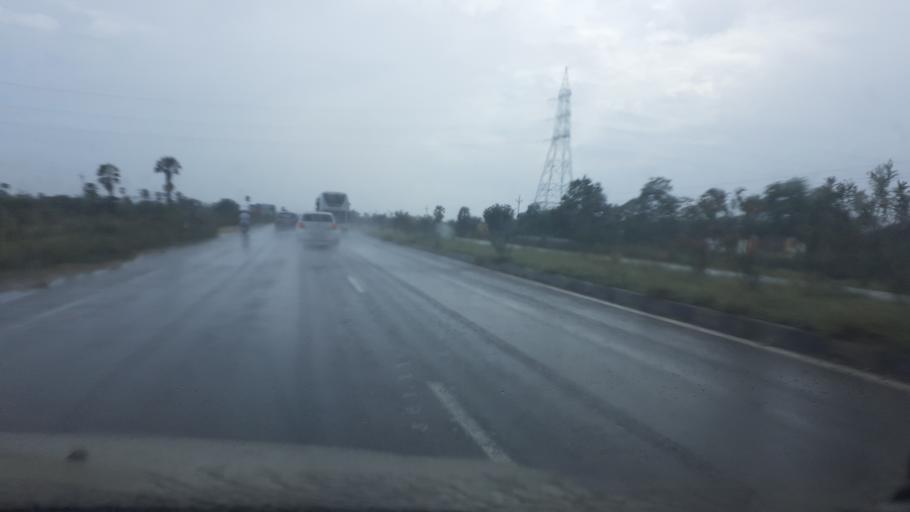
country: IN
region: Tamil Nadu
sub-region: Thoothukkudi
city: Kayattar
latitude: 8.9197
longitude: 77.7655
